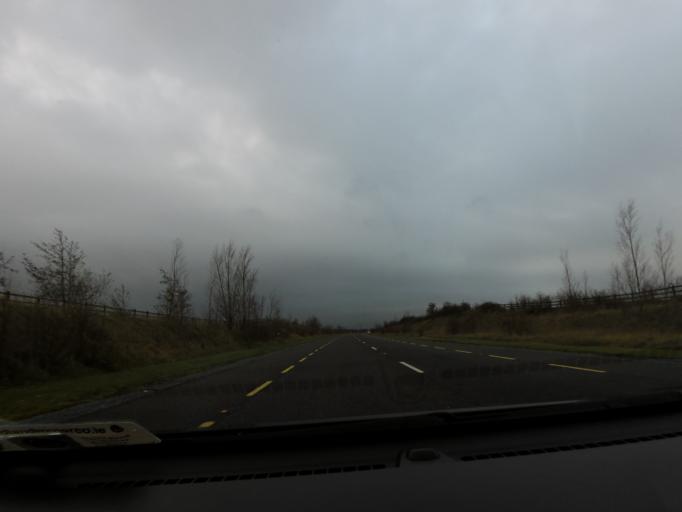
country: IE
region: Connaught
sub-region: County Galway
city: Loughrea
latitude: 53.2494
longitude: -8.5945
